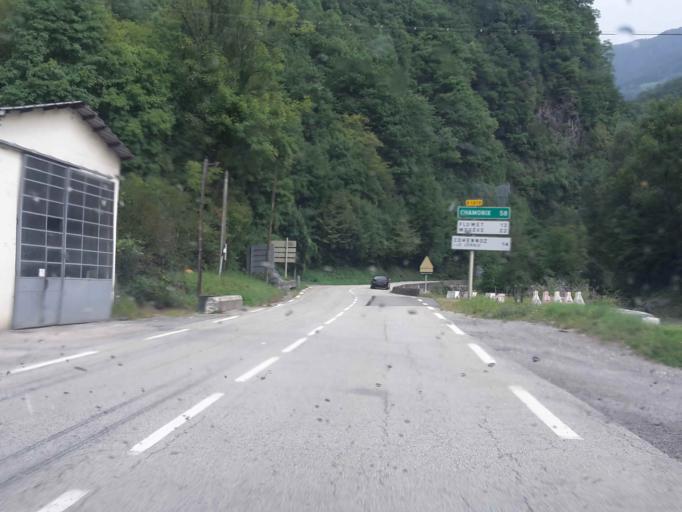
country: FR
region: Rhone-Alpes
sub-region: Departement de la Savoie
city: Ugine
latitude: 45.7516
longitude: 6.4350
